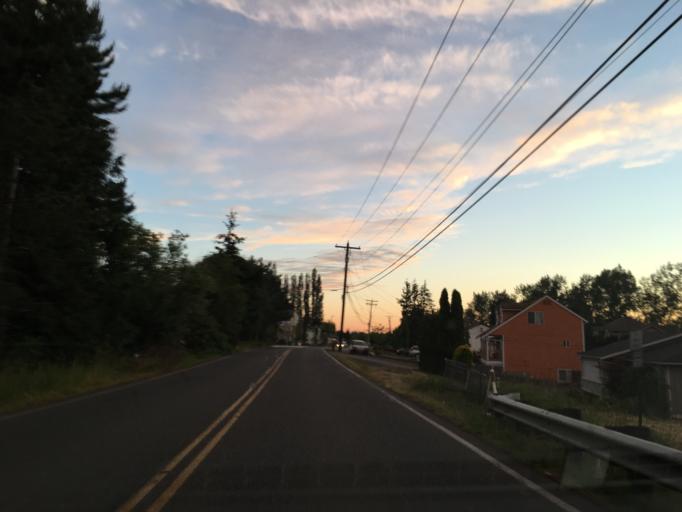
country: US
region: Washington
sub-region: Whatcom County
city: Bellingham
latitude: 48.7855
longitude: -122.4733
